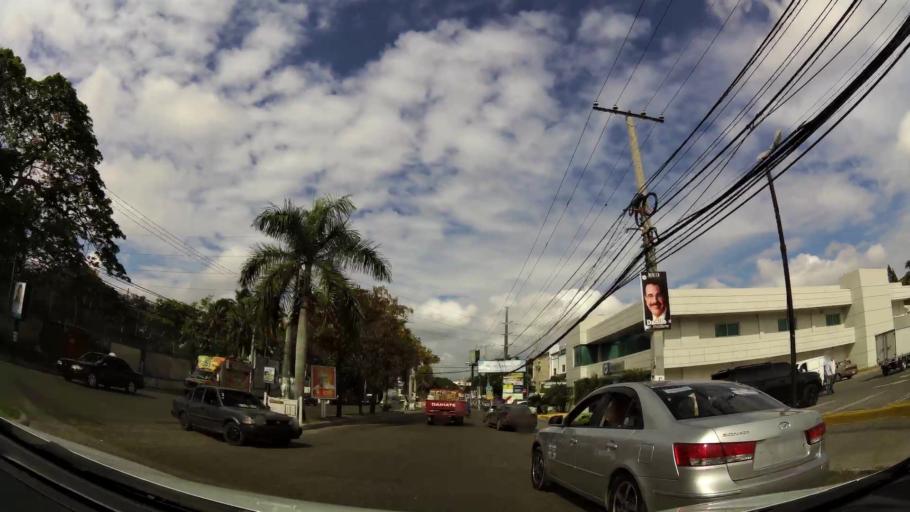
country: DO
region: Santiago
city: Santiago de los Caballeros
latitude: 19.4607
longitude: -70.6839
